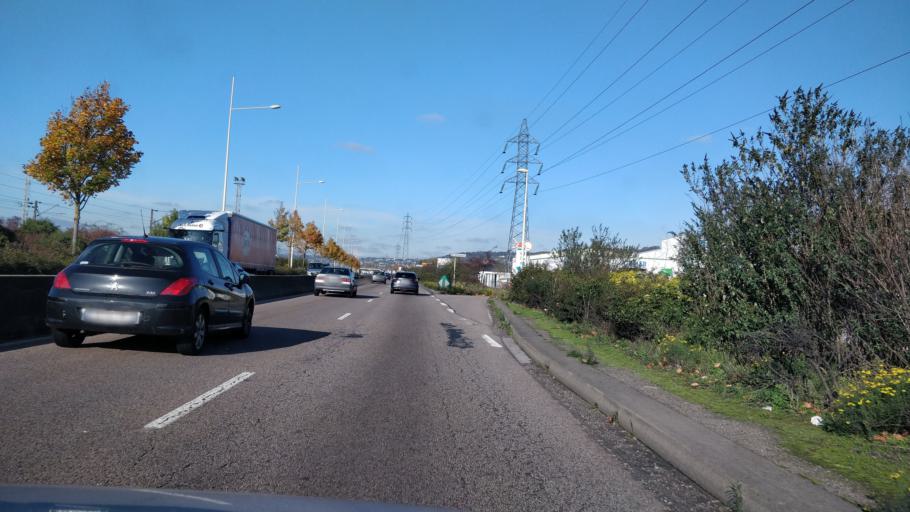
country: FR
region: Haute-Normandie
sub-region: Departement de la Seine-Maritime
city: Saint-Etienne-du-Rouvray
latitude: 49.3975
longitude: 1.1117
